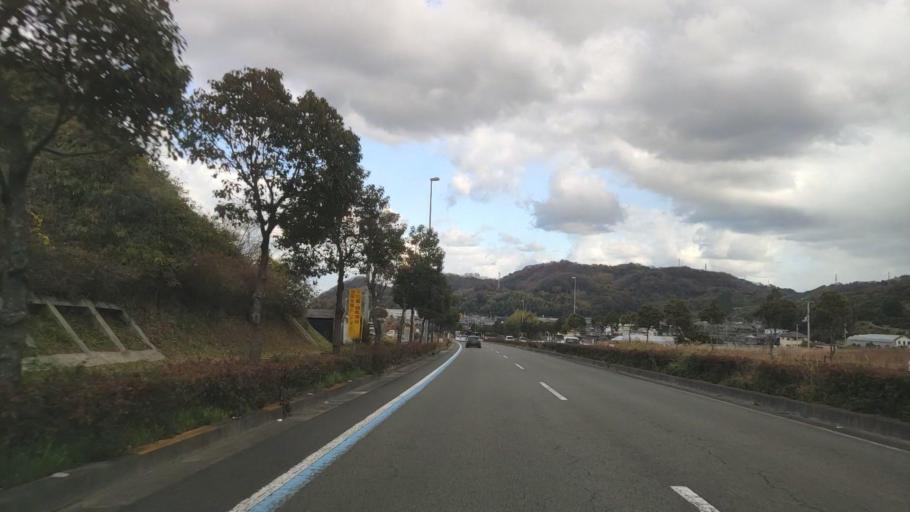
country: JP
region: Ehime
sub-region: Shikoku-chuo Shi
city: Matsuyama
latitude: 33.8936
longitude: 132.7579
